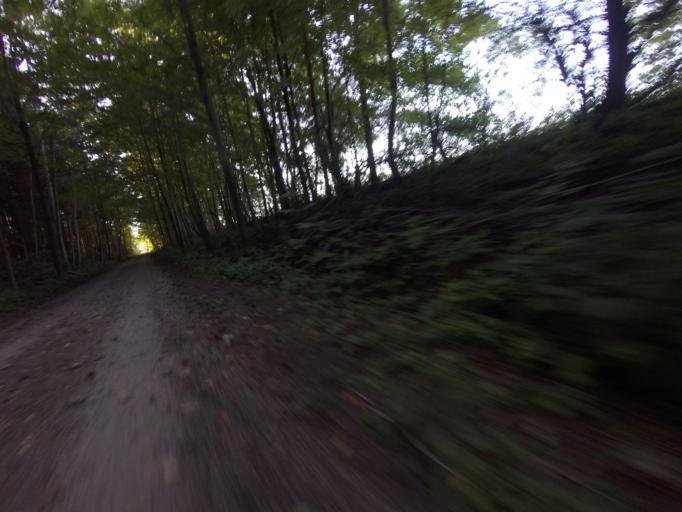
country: CA
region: Ontario
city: Goderich
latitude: 43.7491
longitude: -81.6519
